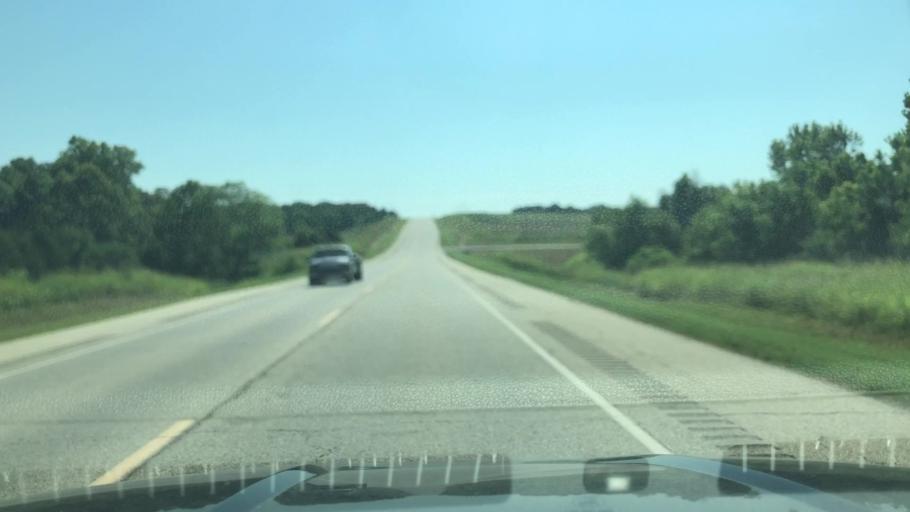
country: US
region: Oklahoma
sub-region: Creek County
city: Mannford
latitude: 36.0031
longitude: -96.4245
